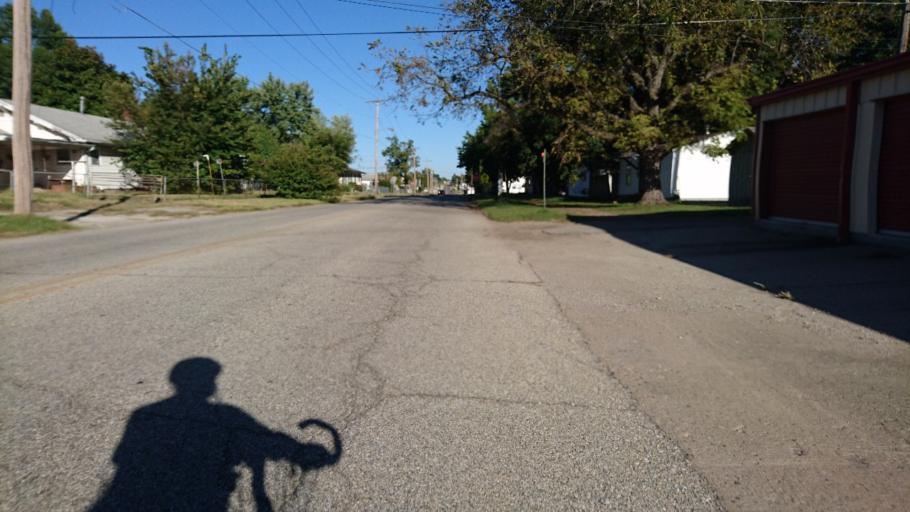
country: US
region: Oklahoma
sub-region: Ottawa County
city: Miami
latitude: 36.8746
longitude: -94.8709
